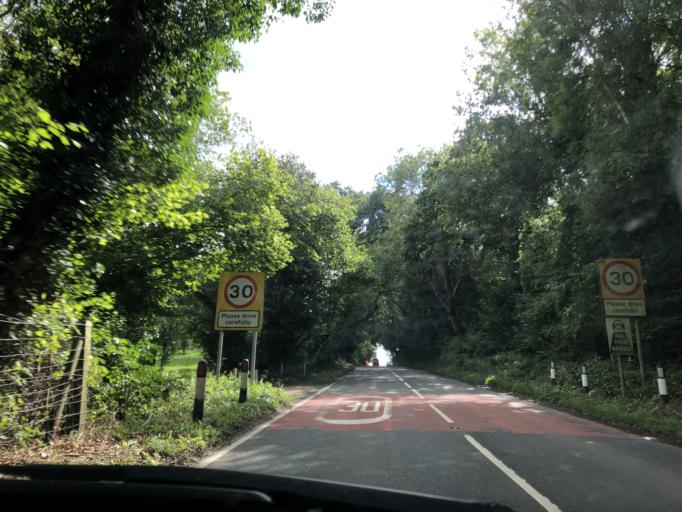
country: GB
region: England
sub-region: East Sussex
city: Forest Row
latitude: 51.0374
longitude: 0.0557
